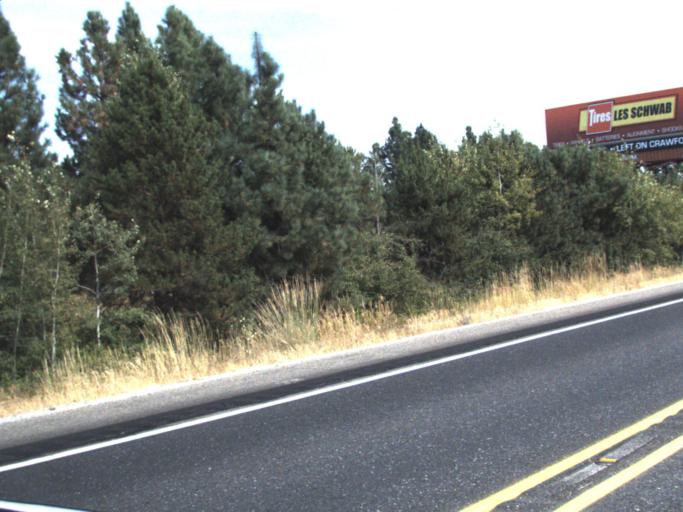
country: US
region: Washington
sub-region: Spokane County
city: Deer Park
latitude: 47.9936
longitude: -117.5478
